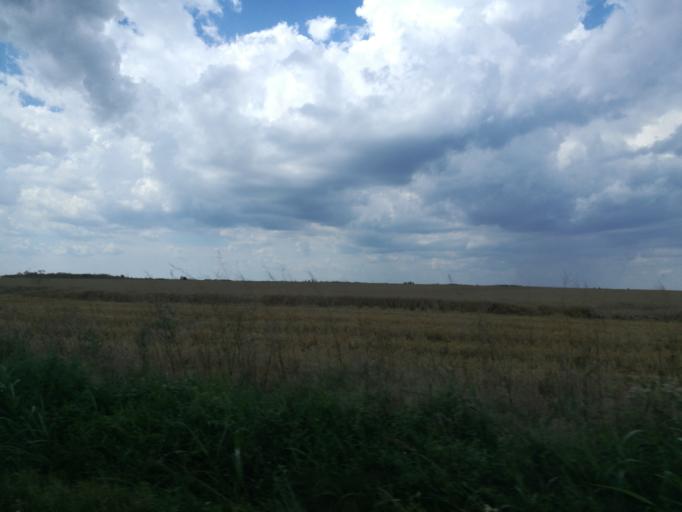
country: RO
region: Constanta
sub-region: Comuna Corbu
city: Corbu
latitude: 44.4241
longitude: 28.6886
